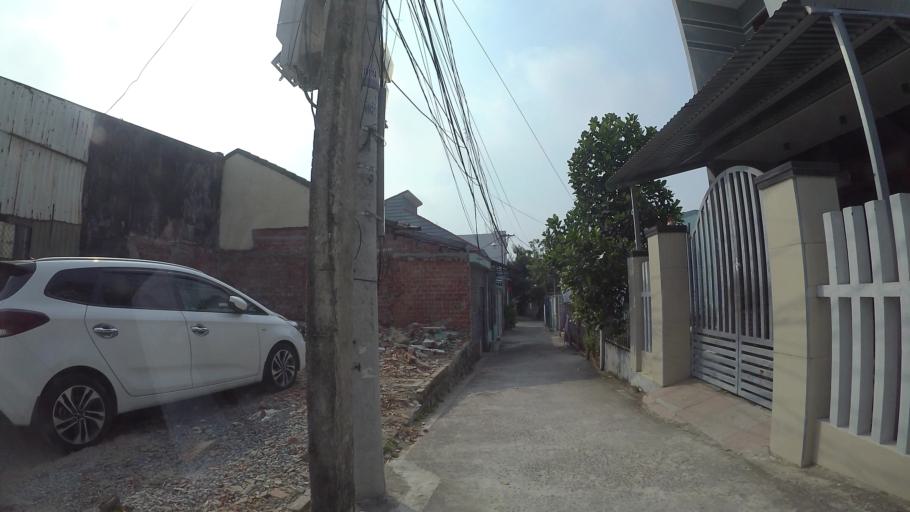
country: VN
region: Da Nang
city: Ngu Hanh Son
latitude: 16.0269
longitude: 108.2452
